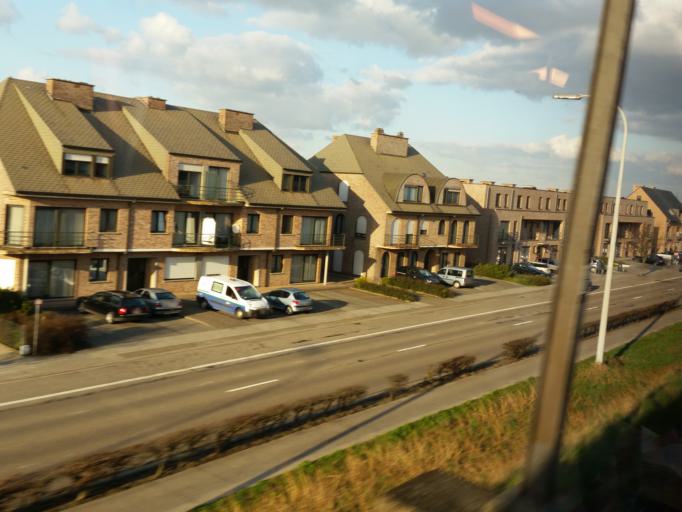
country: BE
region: Flanders
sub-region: Provincie Vlaams-Brabant
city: Kapelle-op-den-Bos
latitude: 51.0116
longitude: 4.3759
